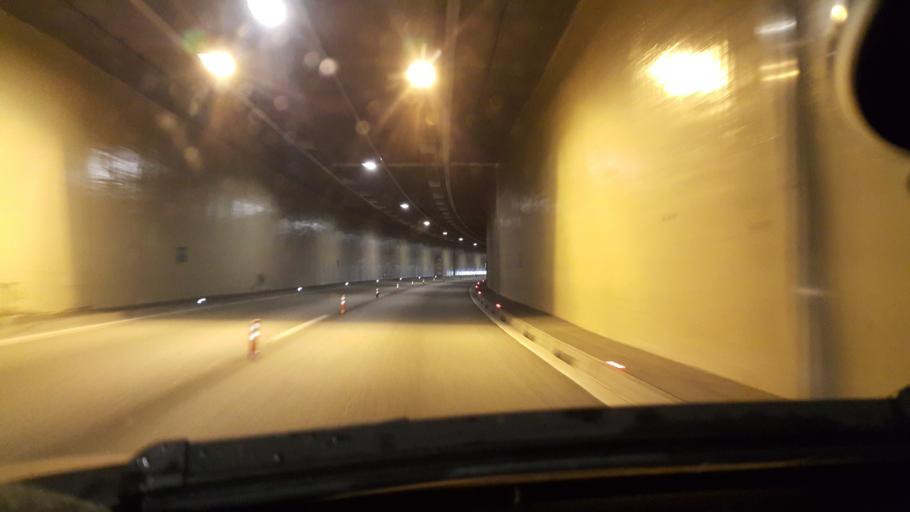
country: AT
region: Carinthia
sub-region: Klagenfurt am Woerthersee
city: Klagenfurt am Woerthersee
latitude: 46.6483
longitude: 14.3297
